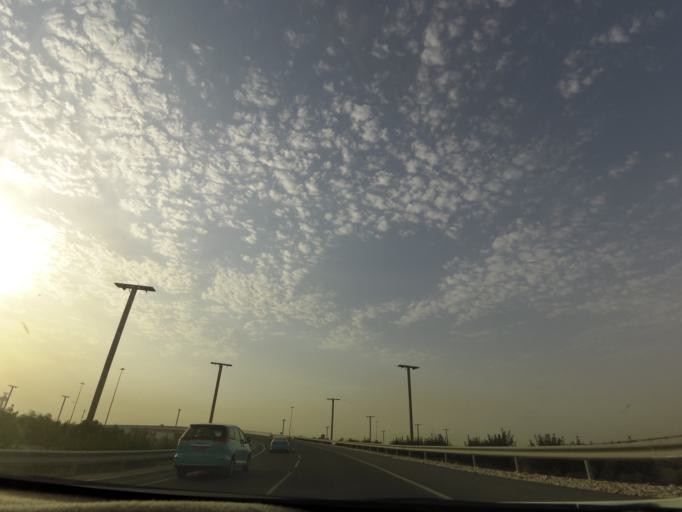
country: QA
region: Al Wakrah
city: Al Wakrah
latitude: 25.2385
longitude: 51.5899
